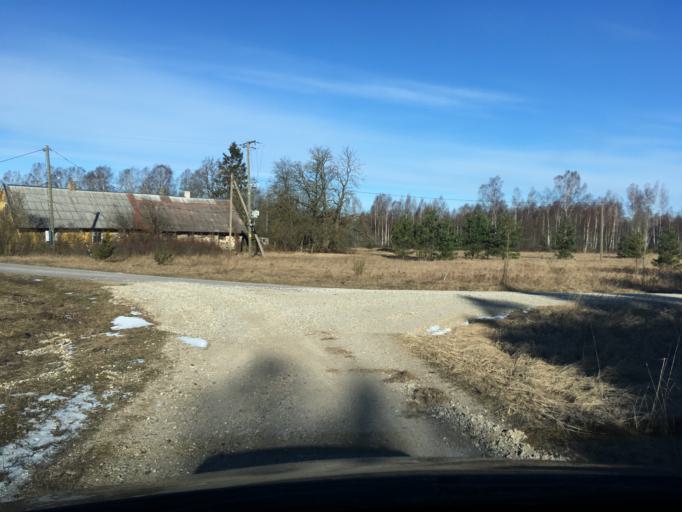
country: EE
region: Laeaene
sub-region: Lihula vald
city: Lihula
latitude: 58.5856
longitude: 23.7131
